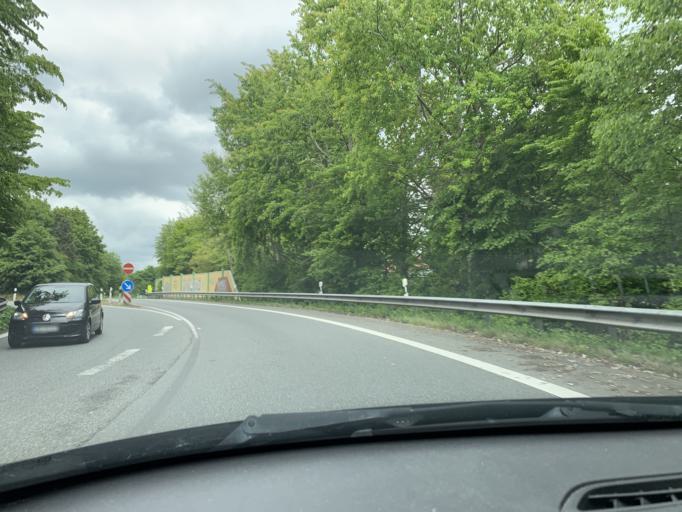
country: DE
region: Lower Saxony
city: Oldenburg
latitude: 53.1441
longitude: 8.1932
